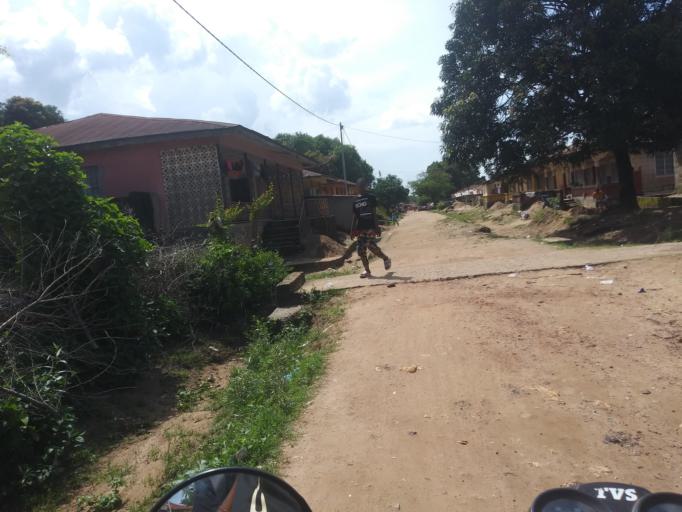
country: SL
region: Northern Province
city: Makeni
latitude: 8.8856
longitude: -12.0378
